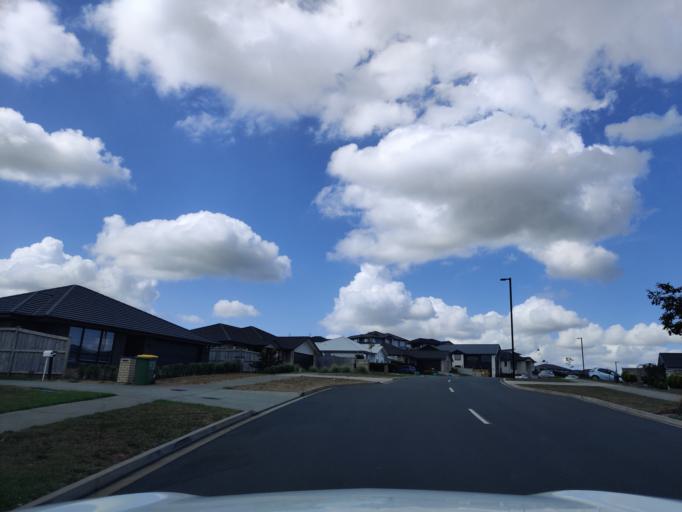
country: NZ
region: Auckland
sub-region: Auckland
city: Pukekohe East
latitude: -37.2372
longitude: 175.0177
